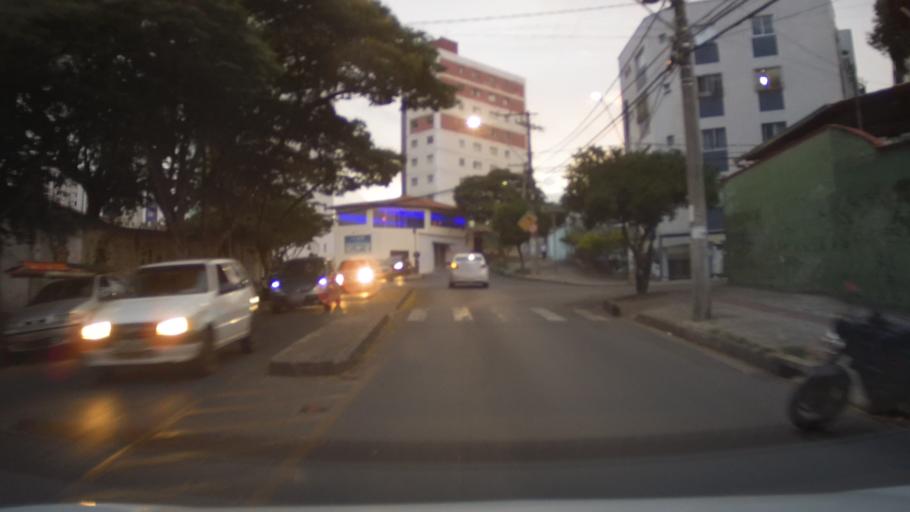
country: BR
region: Minas Gerais
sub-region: Belo Horizonte
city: Belo Horizonte
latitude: -19.8872
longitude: -43.9306
